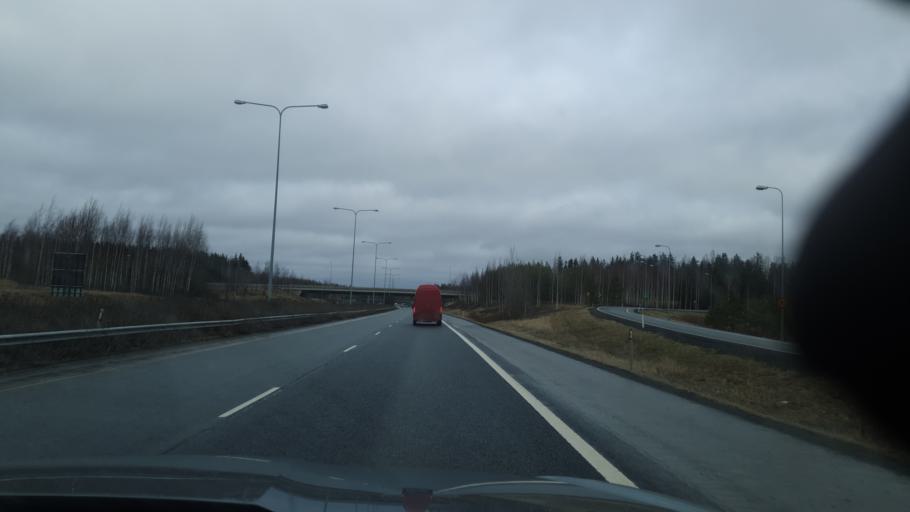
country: FI
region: Pirkanmaa
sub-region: Etelae-Pirkanmaa
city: Toijala
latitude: 61.2198
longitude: 23.8394
